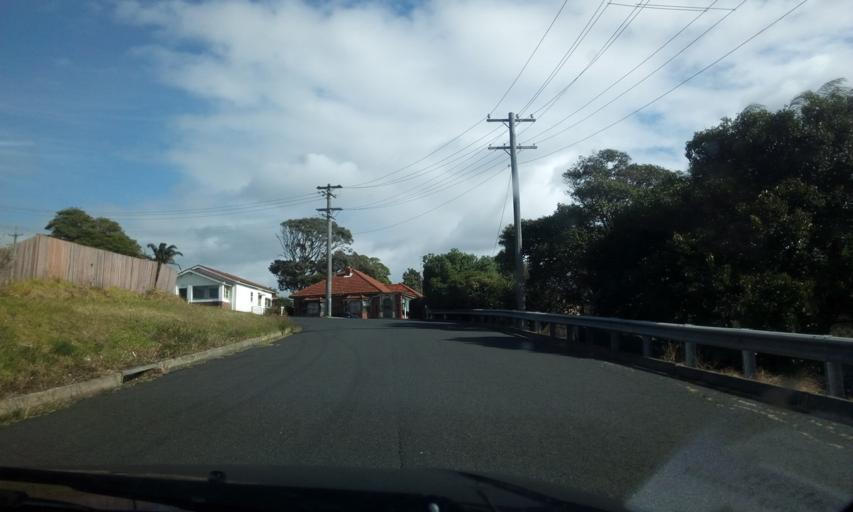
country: AU
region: New South Wales
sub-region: Wollongong
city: Port Kembla
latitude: -34.4832
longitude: 150.8975
